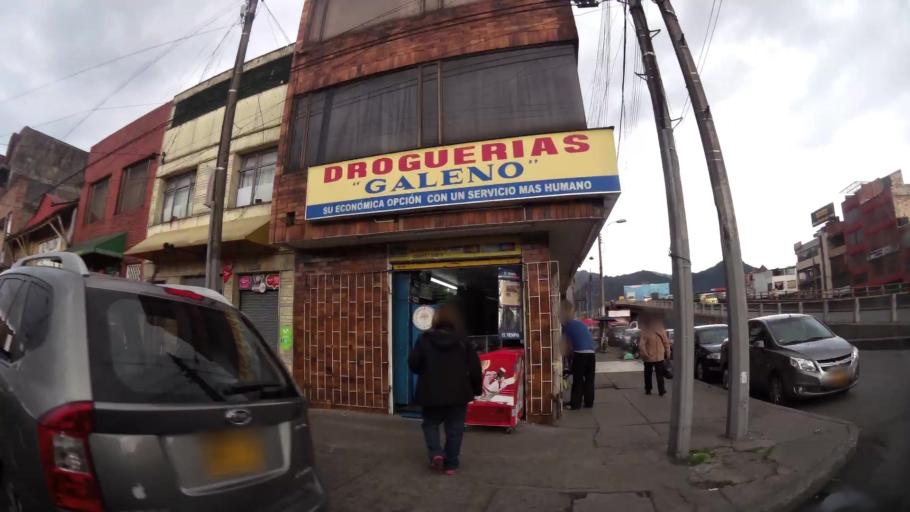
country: CO
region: Bogota D.C.
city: Barrio San Luis
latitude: 4.6687
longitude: -74.0743
